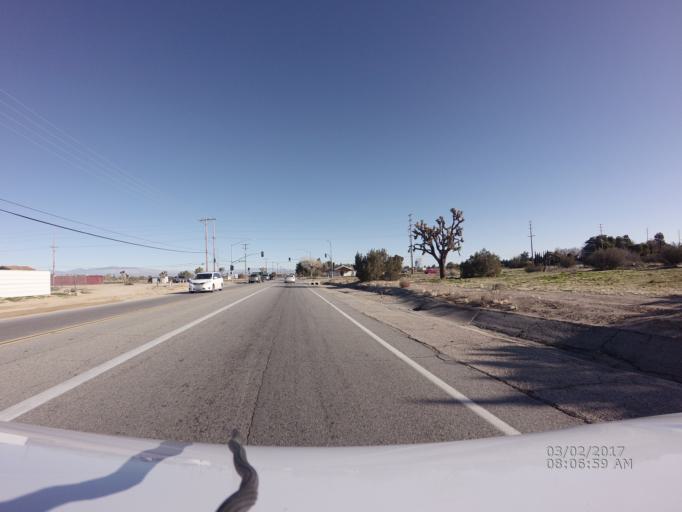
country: US
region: California
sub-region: Los Angeles County
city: Quartz Hill
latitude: 34.6304
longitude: -118.1834
